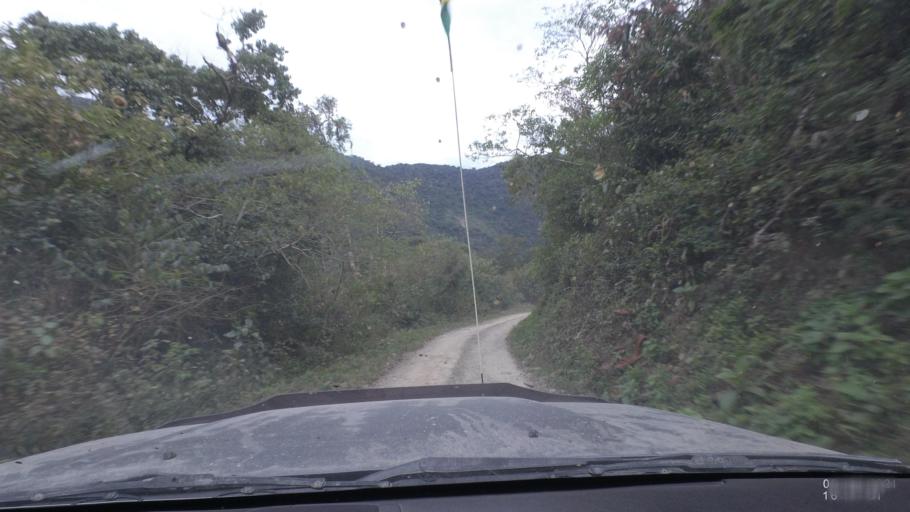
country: BO
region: La Paz
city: Quime
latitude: -16.5289
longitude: -66.7541
